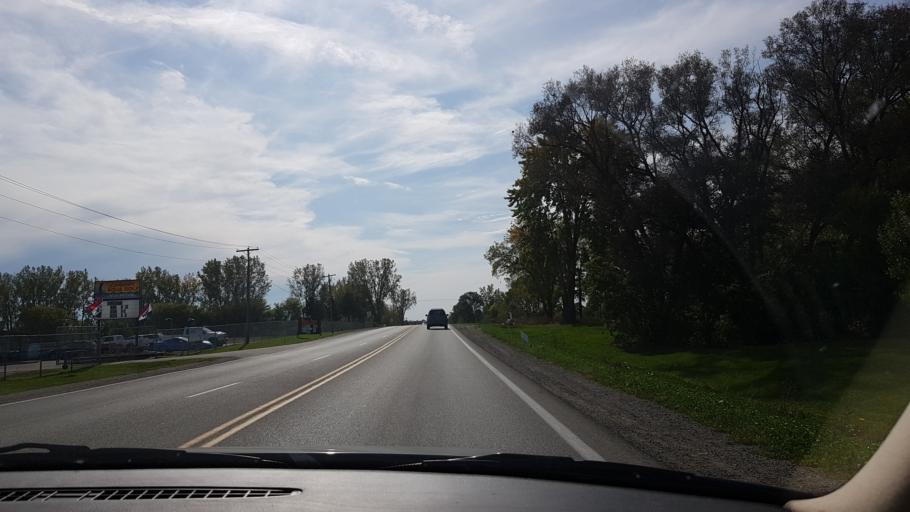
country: CA
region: Ontario
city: Delaware
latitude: 42.9504
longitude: -81.4239
